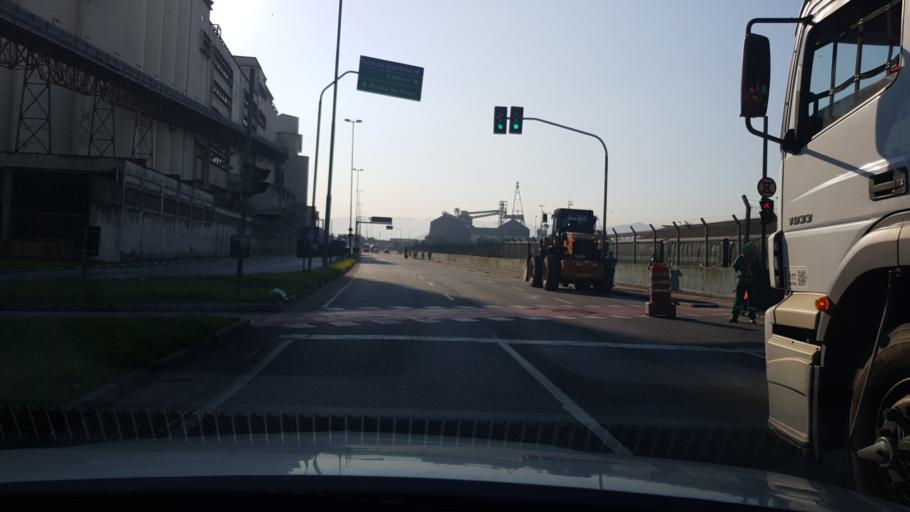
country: BR
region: Sao Paulo
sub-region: Santos
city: Santos
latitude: -23.9607
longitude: -46.3061
